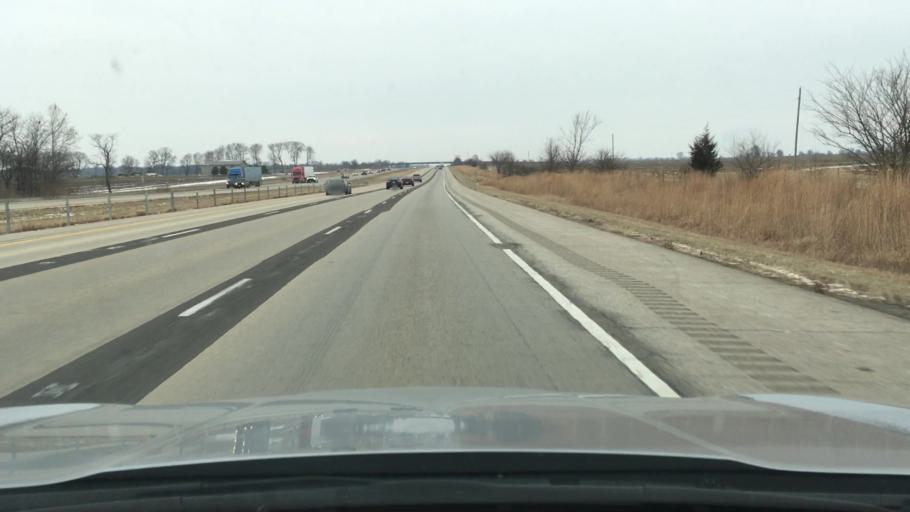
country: US
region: Illinois
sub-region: Sangamon County
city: Chatham
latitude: 39.6372
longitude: -89.6470
